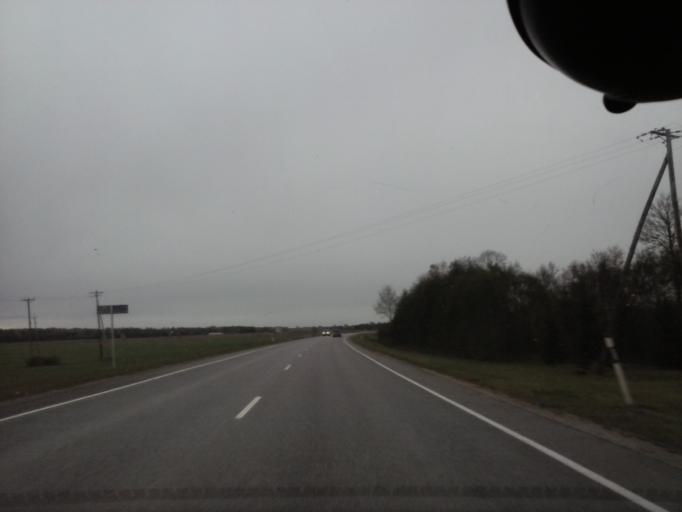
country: EE
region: Jogevamaa
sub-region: Poltsamaa linn
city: Poltsamaa
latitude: 58.7259
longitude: 25.7639
